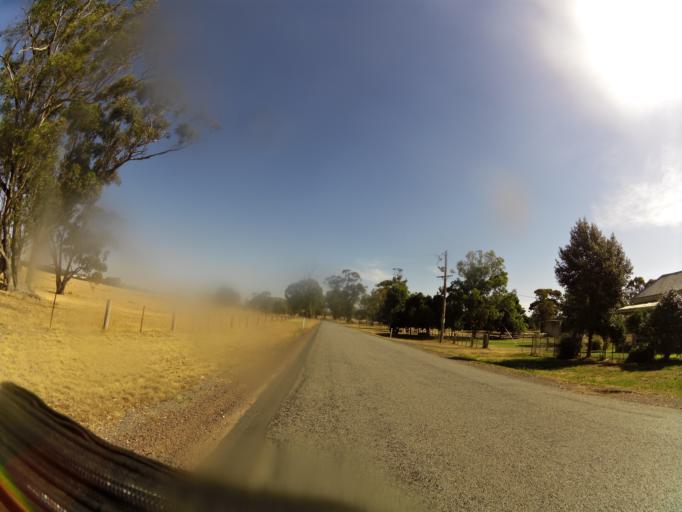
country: AU
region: Victoria
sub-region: Campaspe
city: Kyabram
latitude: -36.8933
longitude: 145.1068
